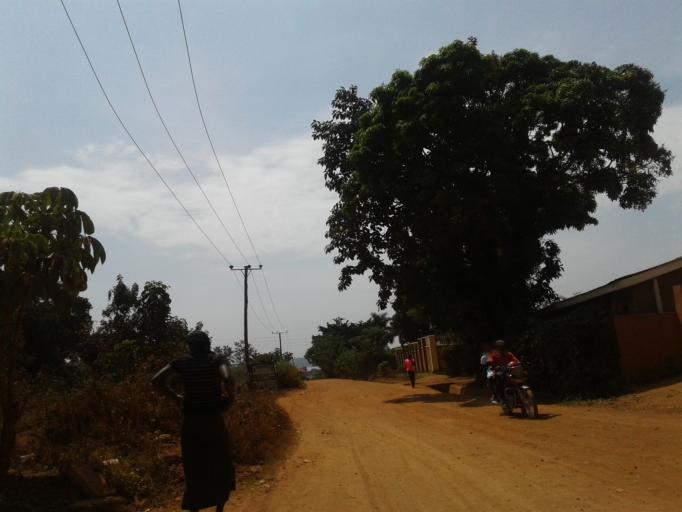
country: UG
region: Central Region
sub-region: Kampala District
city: Kampala
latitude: 0.2613
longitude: 32.6329
